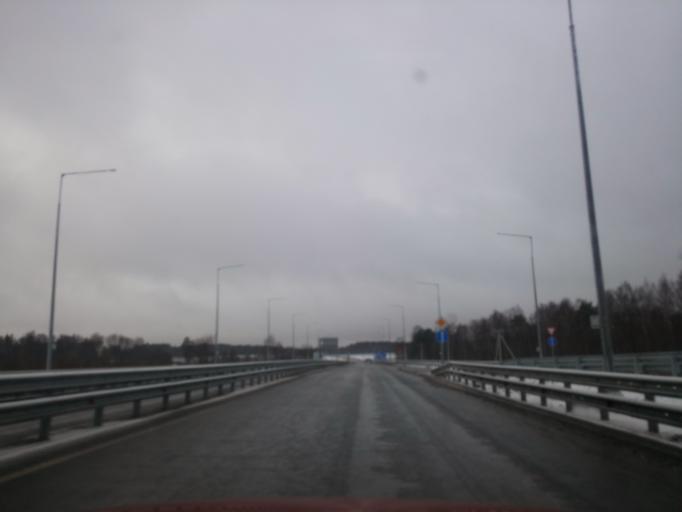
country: RU
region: Tverskaya
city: Likhoslavl'
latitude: 56.9489
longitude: 35.5100
